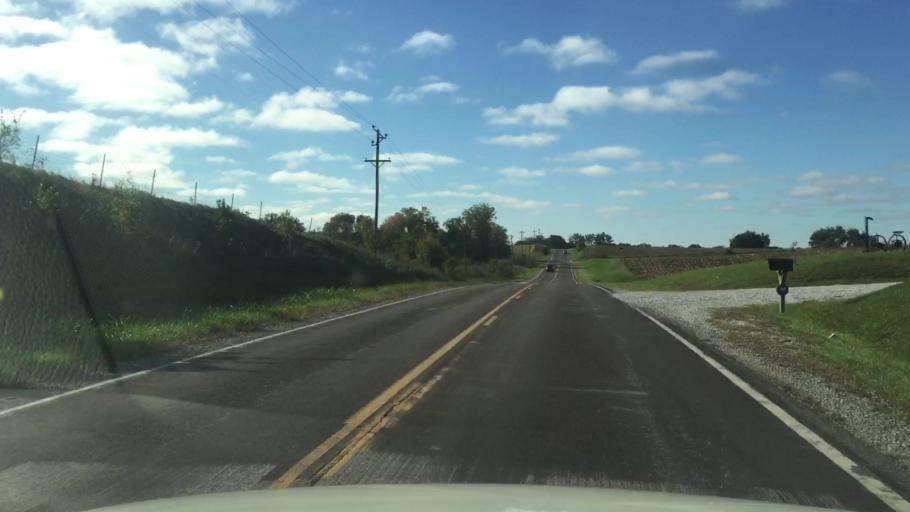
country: US
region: Missouri
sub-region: Howard County
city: New Franklin
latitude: 39.0708
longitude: -92.7459
